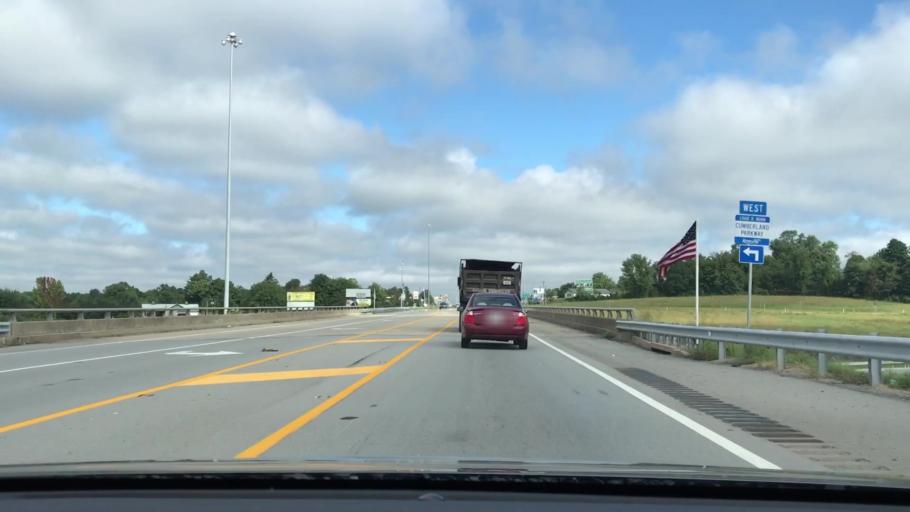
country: US
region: Kentucky
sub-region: Russell County
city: Russell Springs
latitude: 37.0509
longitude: -85.0701
